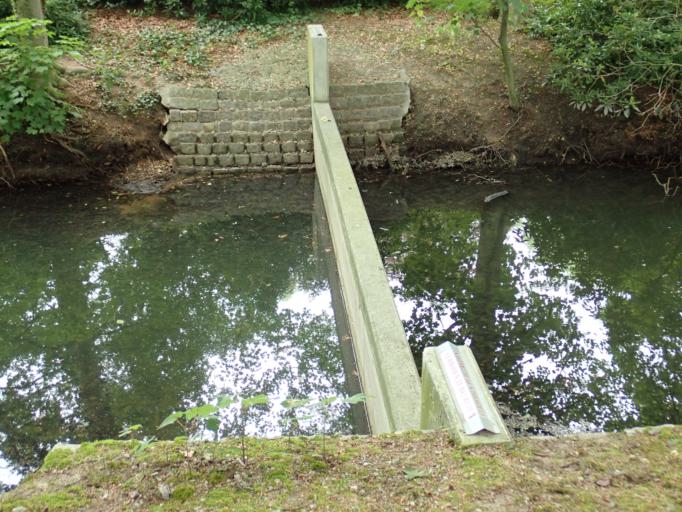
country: BE
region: Flanders
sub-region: Provincie Antwerpen
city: Merksplas
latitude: 51.3676
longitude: 4.8641
